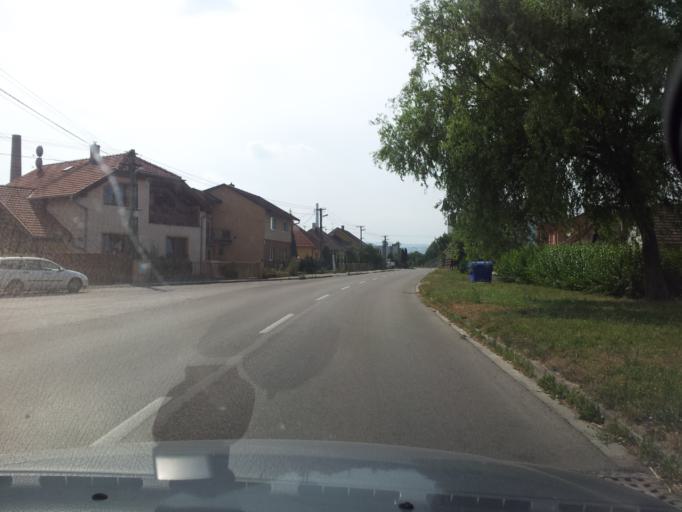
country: SK
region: Trenciansky
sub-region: Okres Trencin
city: Trencin
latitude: 48.8930
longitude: 18.0748
